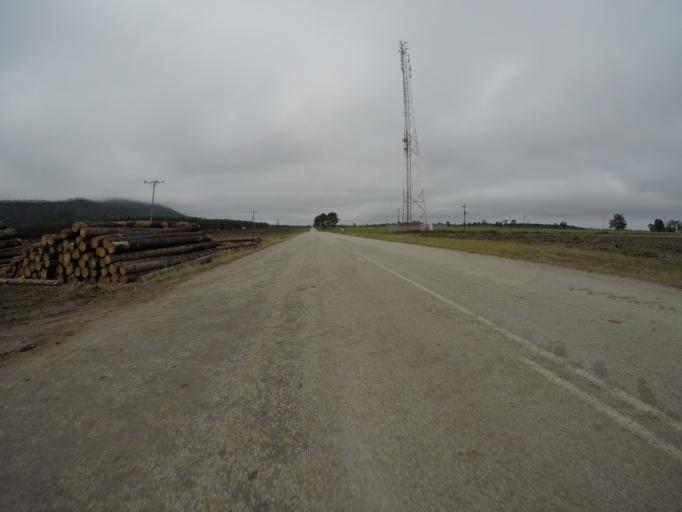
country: ZA
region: Eastern Cape
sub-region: Cacadu District Municipality
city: Kareedouw
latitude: -33.9824
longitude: 24.0541
